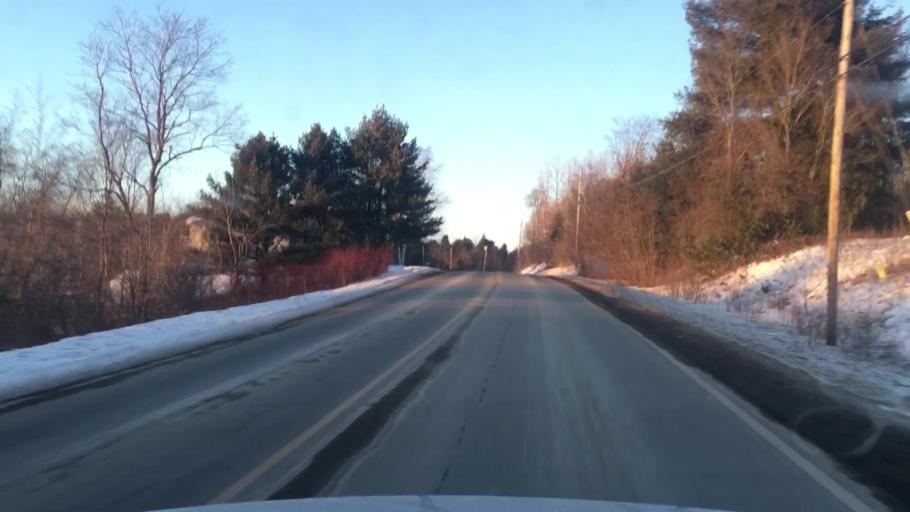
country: US
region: Maine
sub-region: Penobscot County
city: Brewer
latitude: 44.7399
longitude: -68.7651
